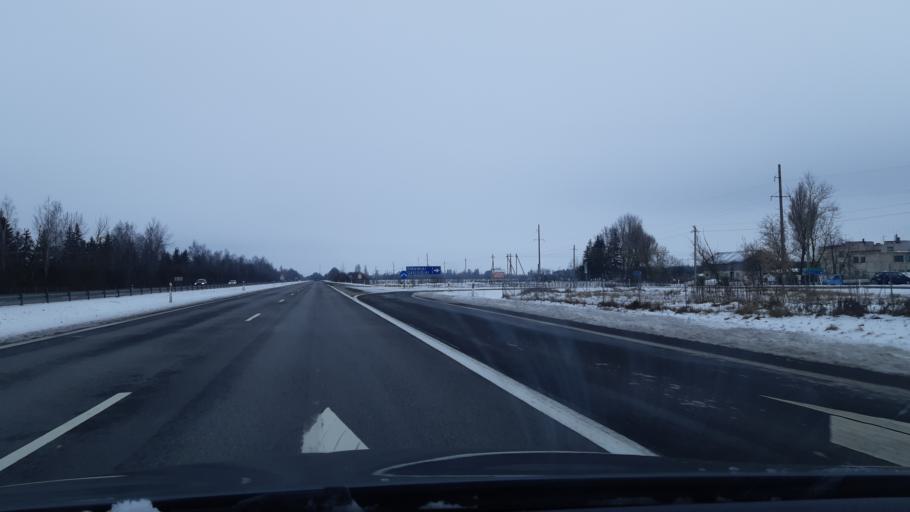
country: LT
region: Kauno apskritis
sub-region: Kaunas
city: Sargenai
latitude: 55.0724
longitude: 23.8149
